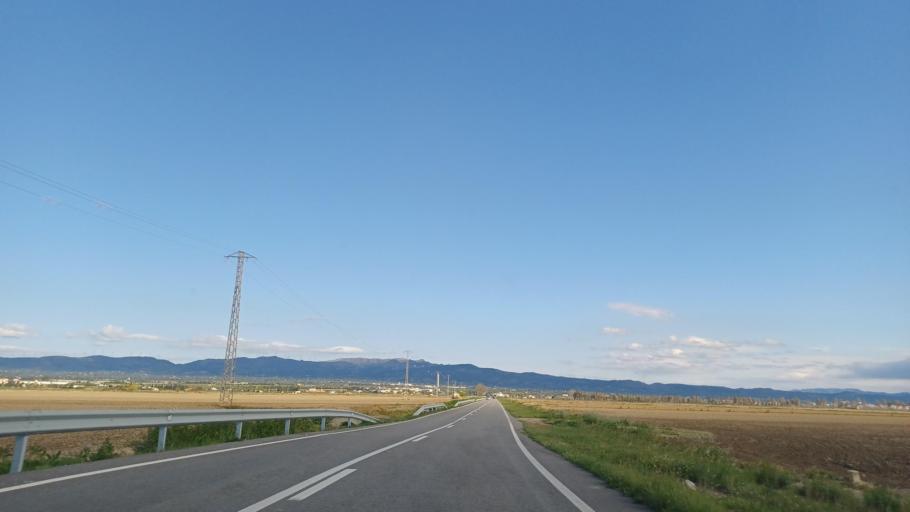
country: ES
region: Catalonia
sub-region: Provincia de Tarragona
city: Camarles
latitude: 40.7657
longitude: 0.6940
